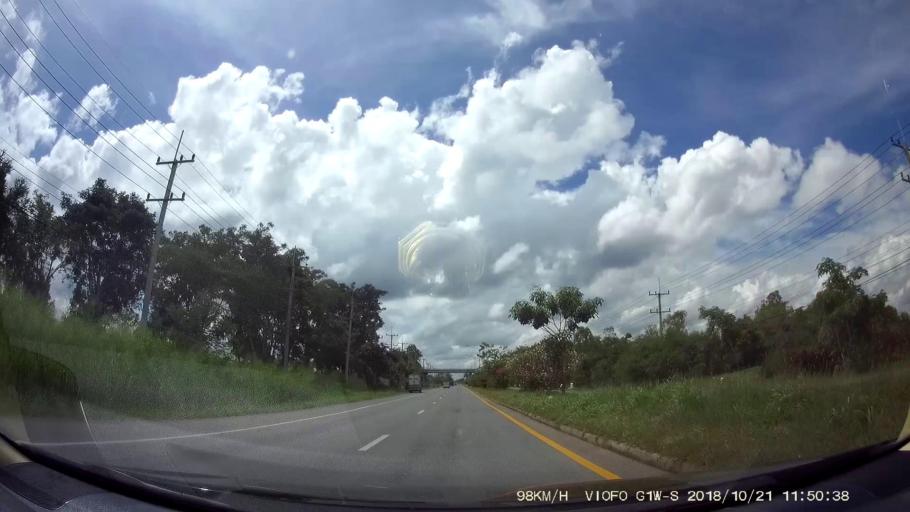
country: TH
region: Chaiyaphum
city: Noen Sa-nga
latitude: 15.6299
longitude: 101.9279
